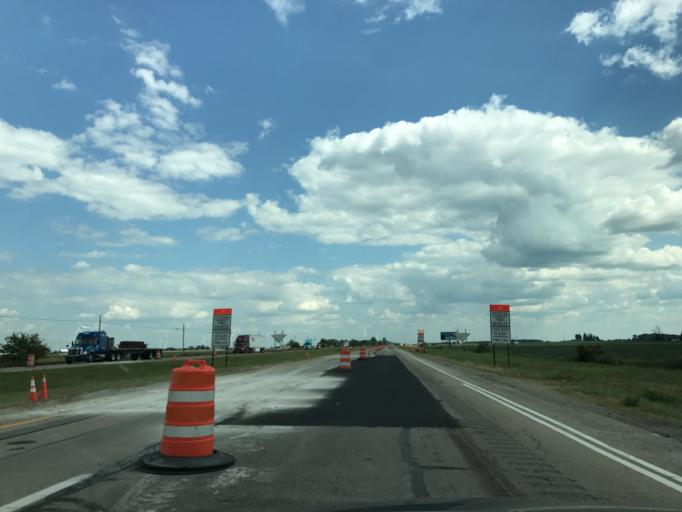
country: US
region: Ohio
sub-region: Van Wert County
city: Convoy
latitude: 40.9520
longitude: -84.7247
